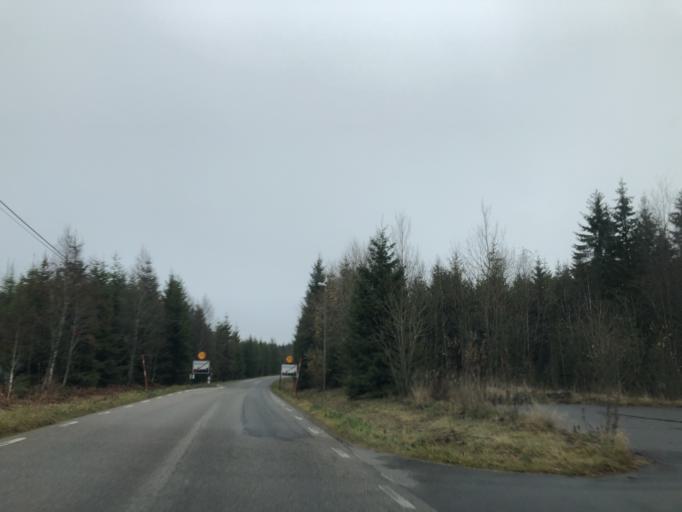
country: SE
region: Vaestra Goetaland
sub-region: Ulricehamns Kommun
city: Ulricehamn
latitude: 57.7036
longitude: 13.5009
